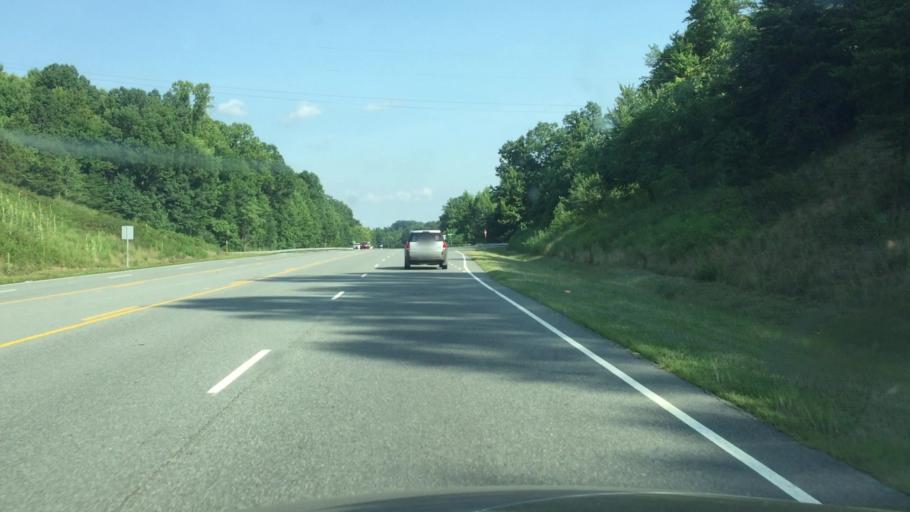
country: US
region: North Carolina
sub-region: Rockingham County
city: Reidsville
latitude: 36.3695
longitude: -79.6454
